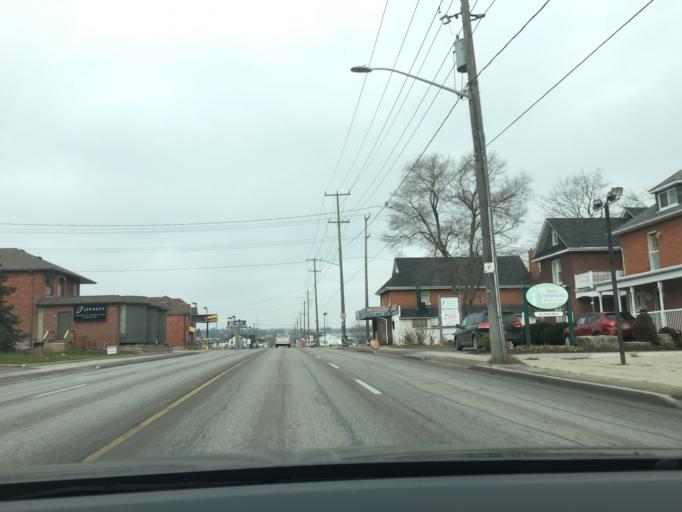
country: CA
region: Ontario
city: Barrie
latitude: 44.3790
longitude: -79.6936
